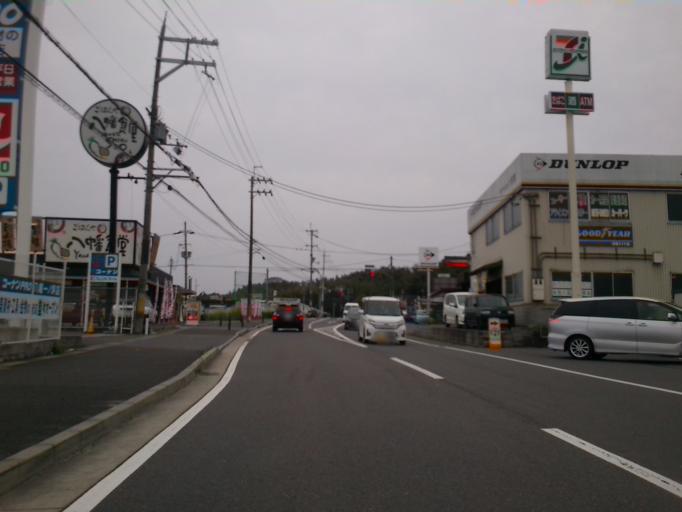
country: JP
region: Kyoto
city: Yawata
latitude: 34.8556
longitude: 135.7142
